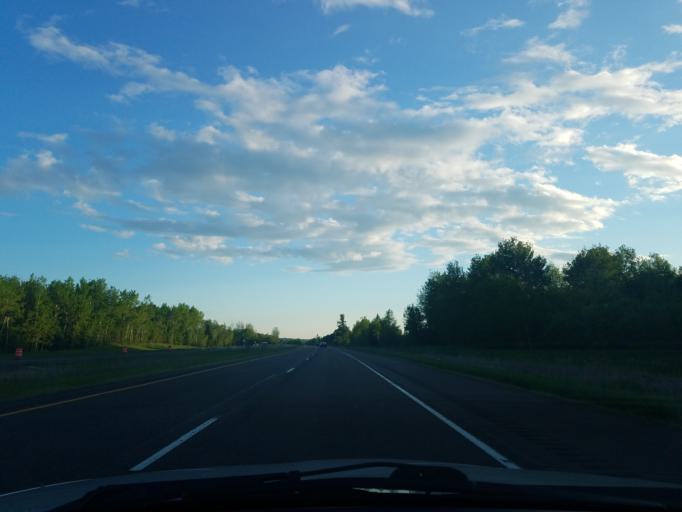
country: US
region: Minnesota
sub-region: Carlton County
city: Carlton
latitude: 46.6223
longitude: -92.5394
